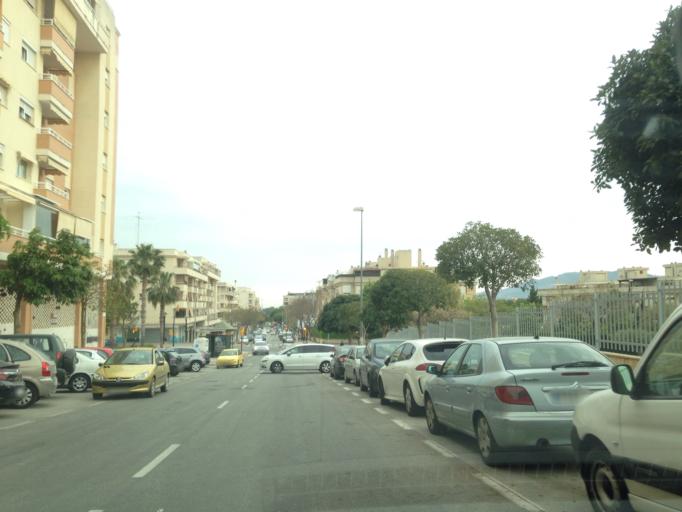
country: ES
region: Andalusia
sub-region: Provincia de Malaga
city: Malaga
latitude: 36.7253
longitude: -4.4799
